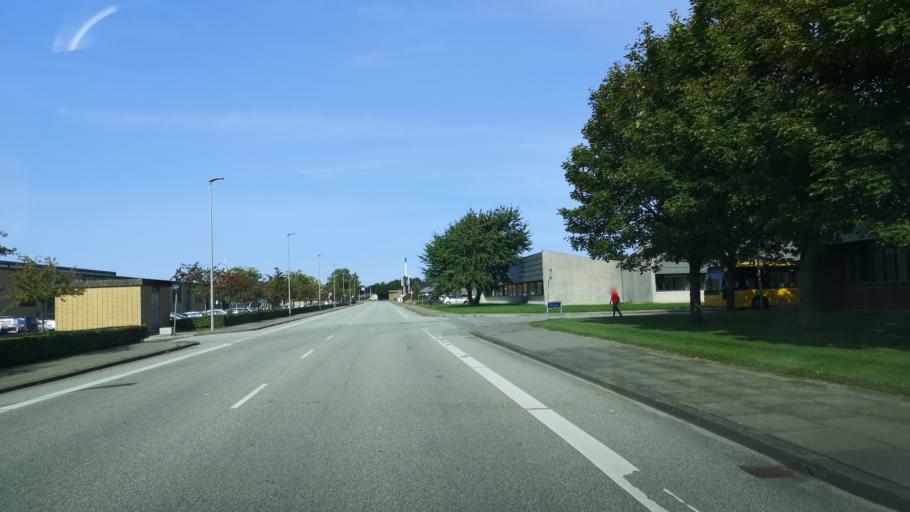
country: DK
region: Central Jutland
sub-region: Herning Kommune
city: Herning
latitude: 56.1507
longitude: 8.9861
